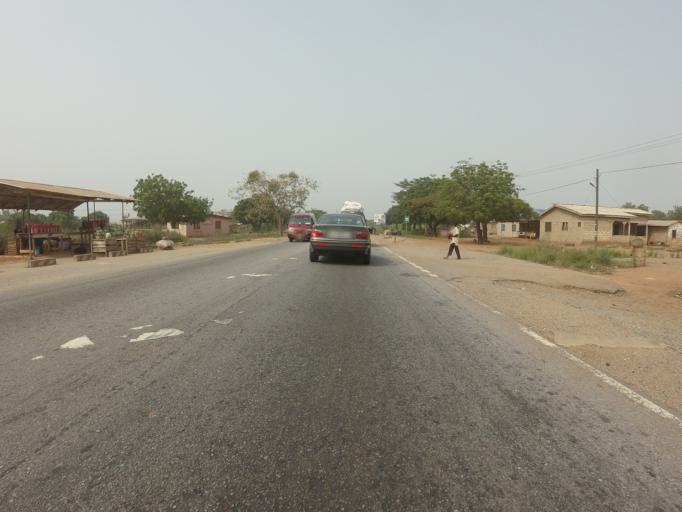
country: GH
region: Volta
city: Anloga
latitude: 5.9549
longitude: 0.5242
